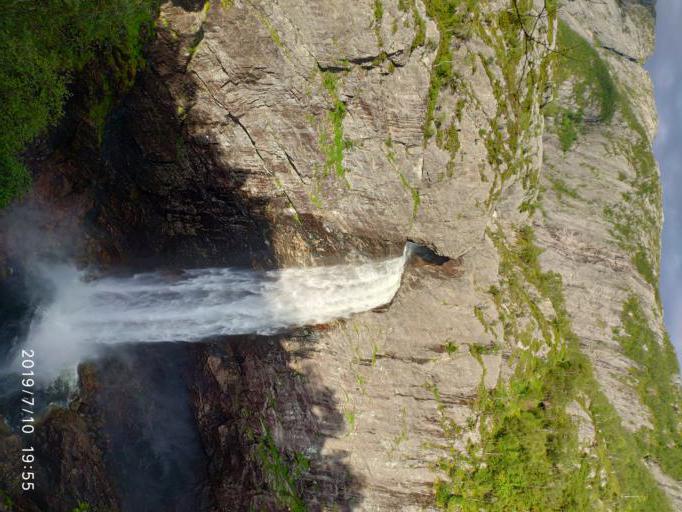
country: NO
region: Rogaland
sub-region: Forsand
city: Forsand
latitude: 58.8579
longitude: 6.3825
